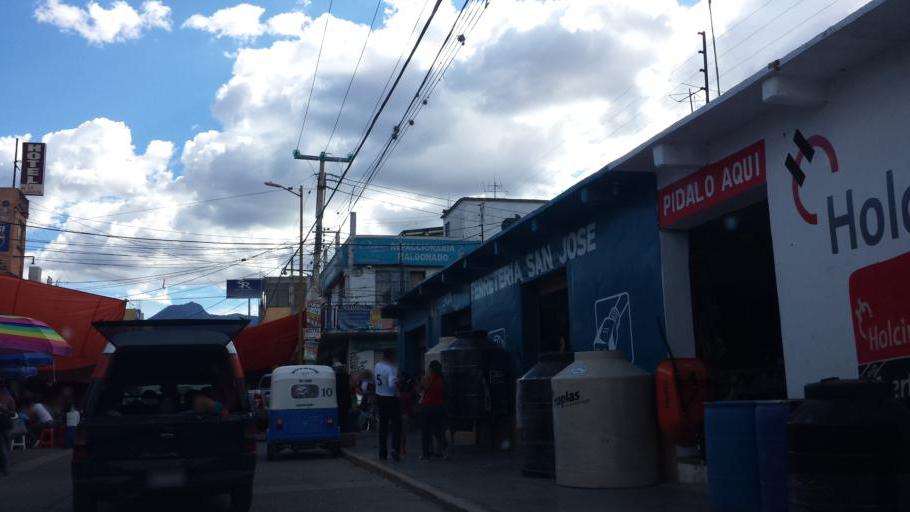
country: MX
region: Oaxaca
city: Tlacolula de Matamoros
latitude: 16.9601
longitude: -96.4775
